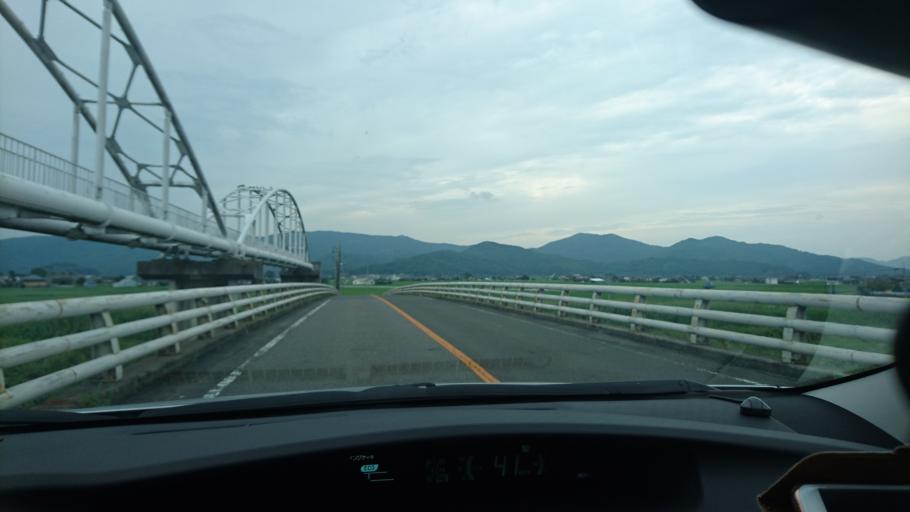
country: JP
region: Saga Prefecture
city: Takeocho-takeo
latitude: 33.2001
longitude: 130.1172
